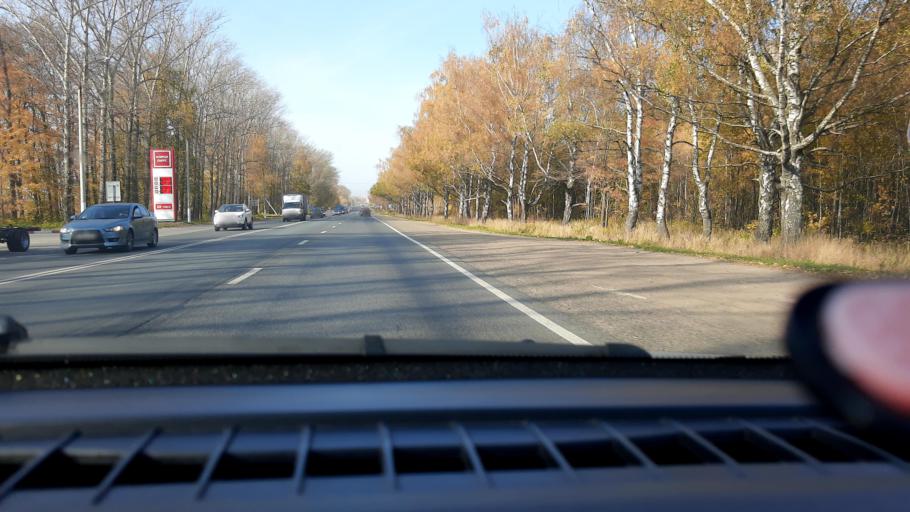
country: RU
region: Nizjnij Novgorod
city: Kstovo
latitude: 56.1373
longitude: 44.2373
